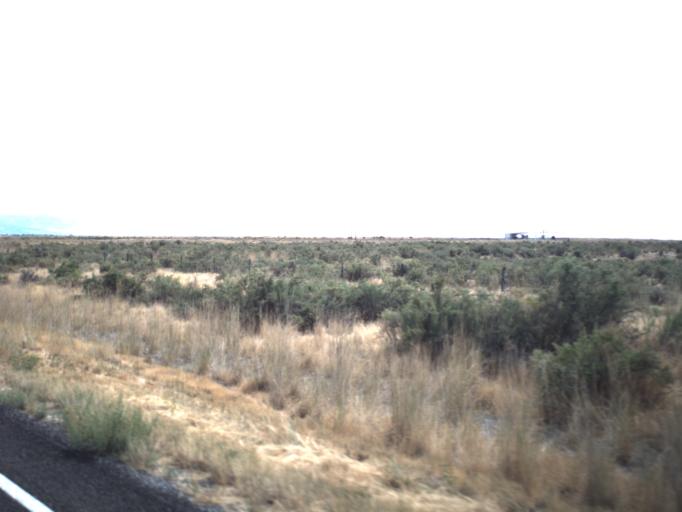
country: US
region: Utah
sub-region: Box Elder County
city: Tremonton
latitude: 41.5922
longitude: -112.2784
